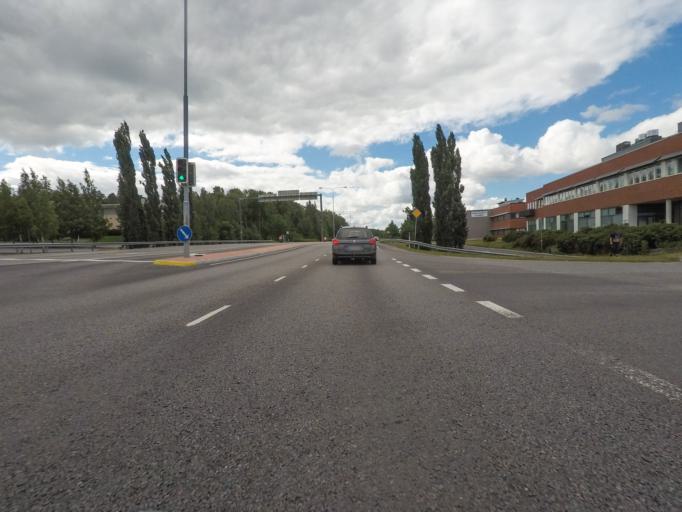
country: FI
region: Varsinais-Suomi
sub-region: Turku
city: Raisio
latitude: 60.4796
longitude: 22.1614
